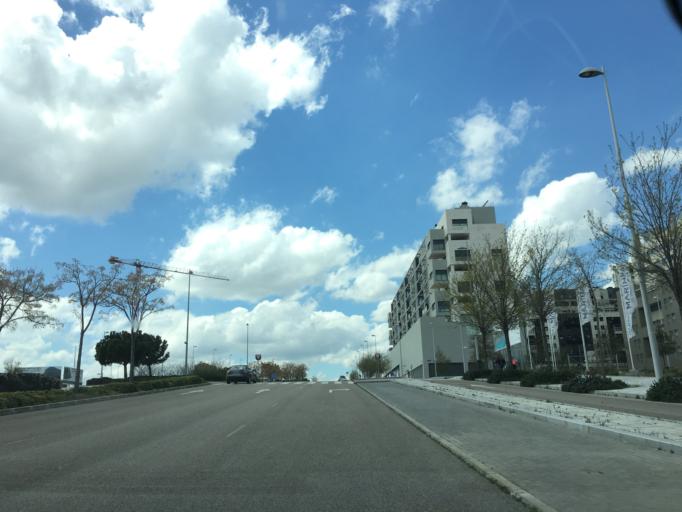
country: ES
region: Madrid
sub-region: Provincia de Madrid
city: Hortaleza
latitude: 40.4941
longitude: -3.6151
